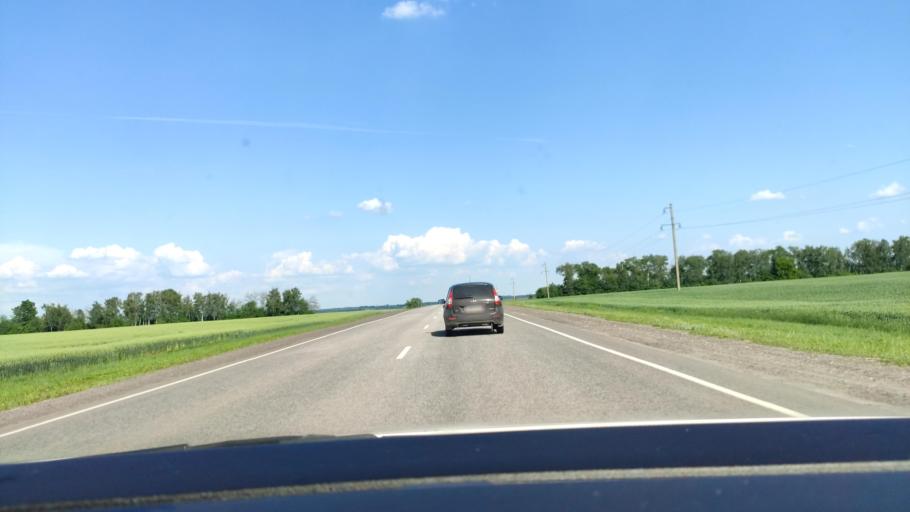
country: RU
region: Voronezj
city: Orlovo
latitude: 51.6842
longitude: 39.5492
